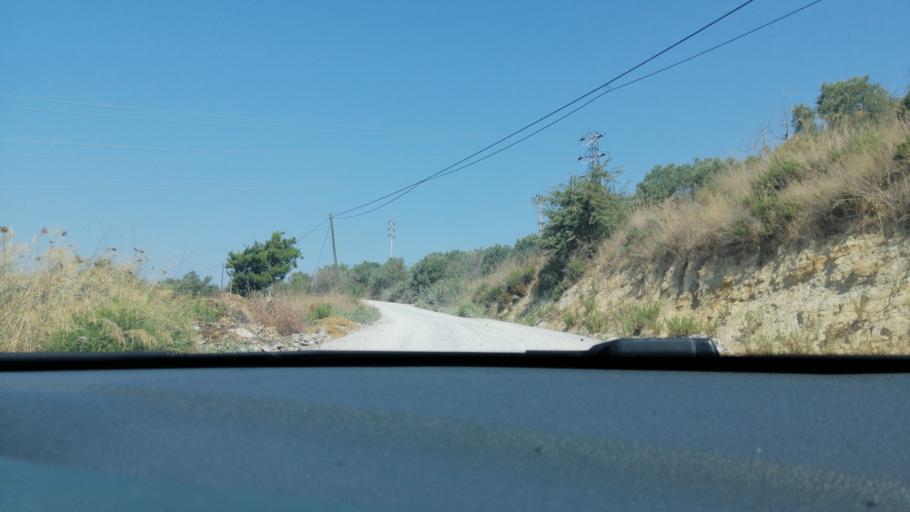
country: TR
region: Aydin
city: Davutlar
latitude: 37.7850
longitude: 27.3160
